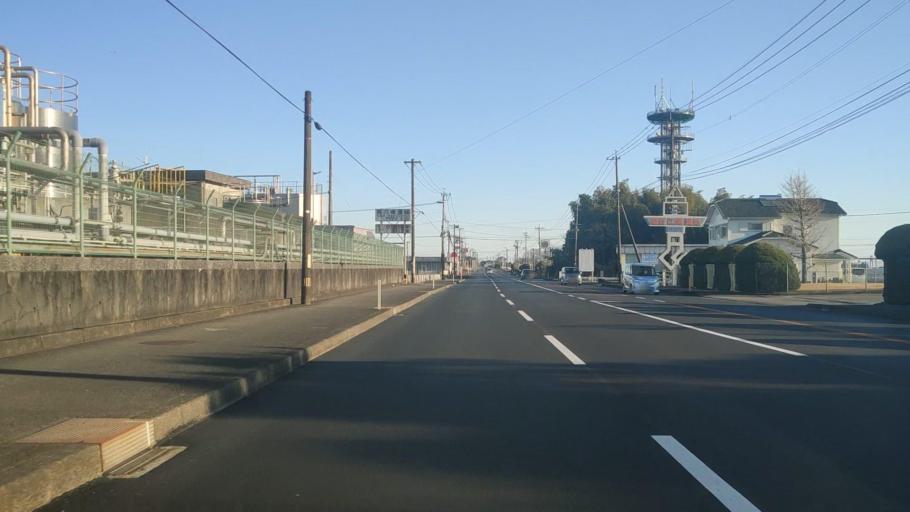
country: JP
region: Miyazaki
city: Takanabe
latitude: 32.2244
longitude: 131.5439
